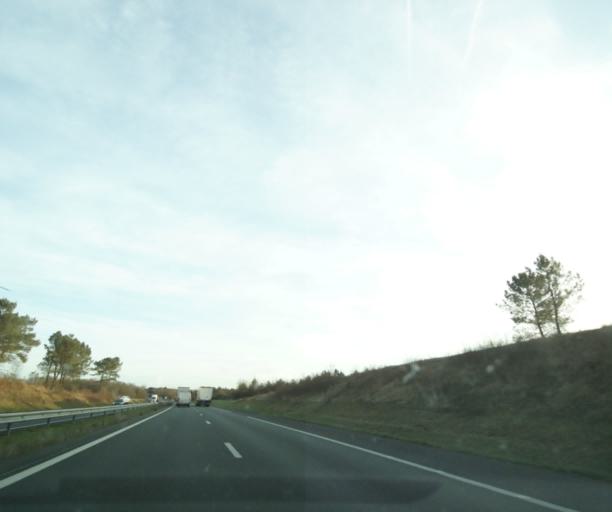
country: FR
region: Aquitaine
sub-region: Departement de la Gironde
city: Pugnac
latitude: 45.0767
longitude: -0.4677
